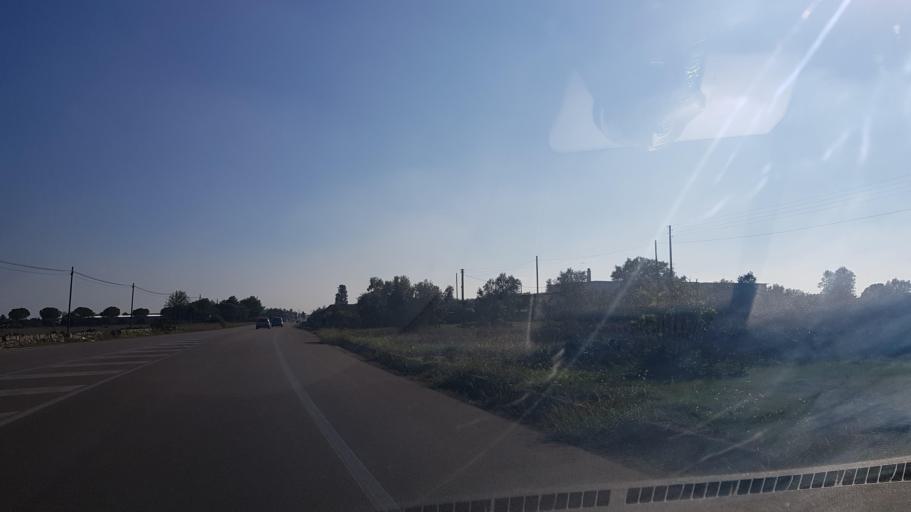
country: IT
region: Apulia
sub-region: Provincia di Lecce
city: Nociglia
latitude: 40.0301
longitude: 18.3248
